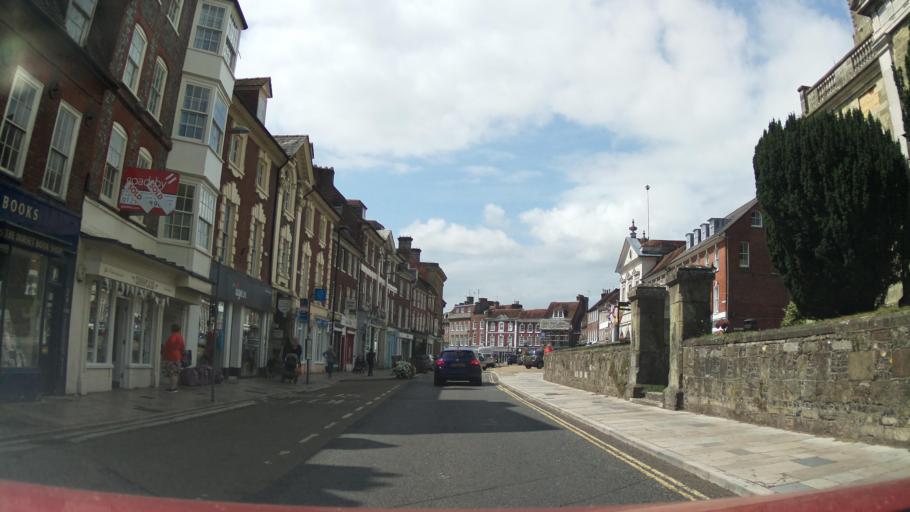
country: GB
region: England
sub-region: Dorset
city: Blandford Forum
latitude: 50.8560
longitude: -2.1637
